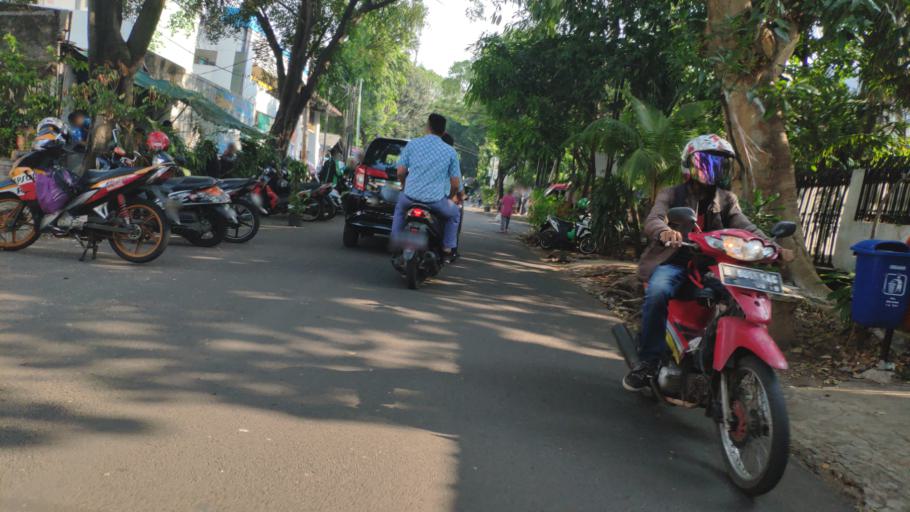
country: ID
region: Jakarta Raya
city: Jakarta
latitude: -6.2468
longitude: 106.8000
